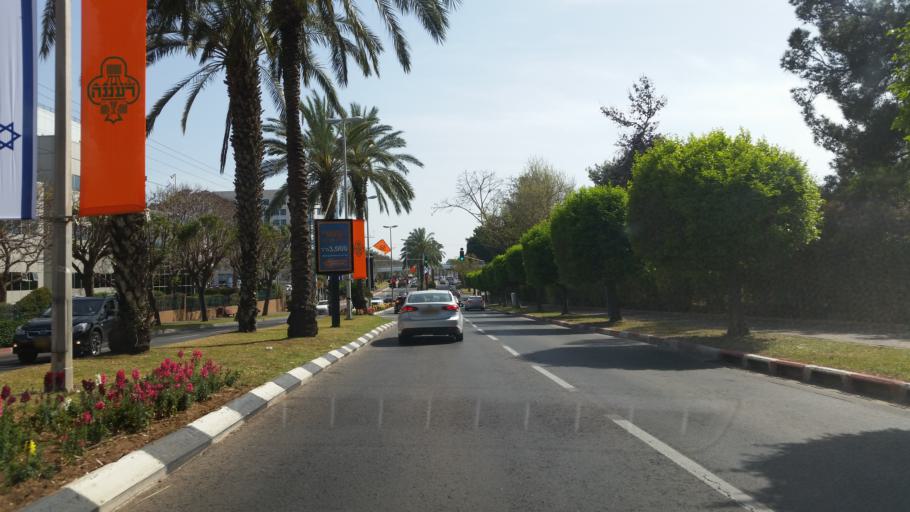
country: IL
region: Central District
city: Ra'anana
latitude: 32.1883
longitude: 34.8548
